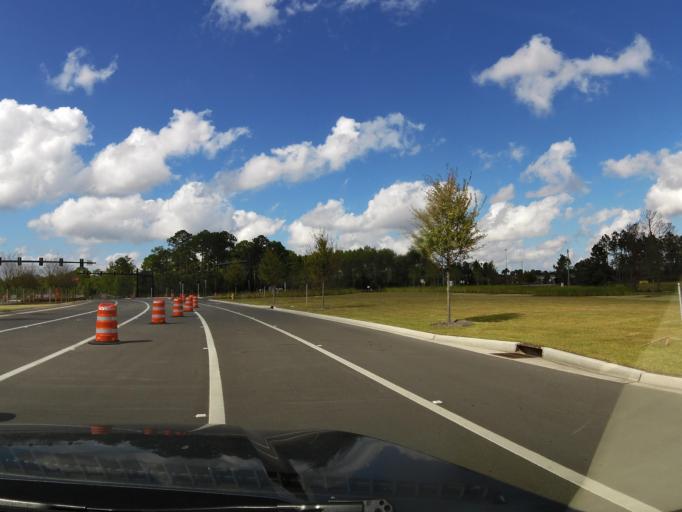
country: US
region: Florida
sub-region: Saint Johns County
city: Ponte Vedra Beach
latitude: 30.2484
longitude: -81.4993
